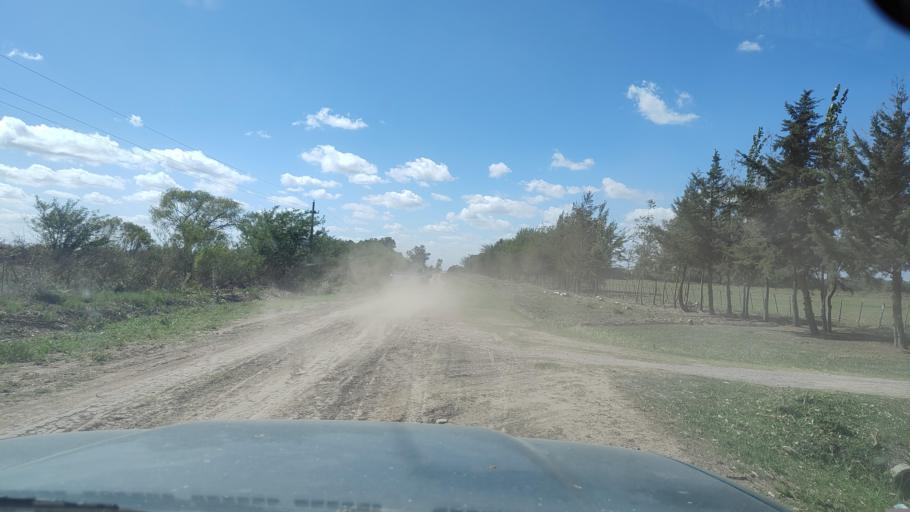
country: AR
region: Buenos Aires
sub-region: Partido de Lujan
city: Lujan
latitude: -34.5321
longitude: -59.1498
